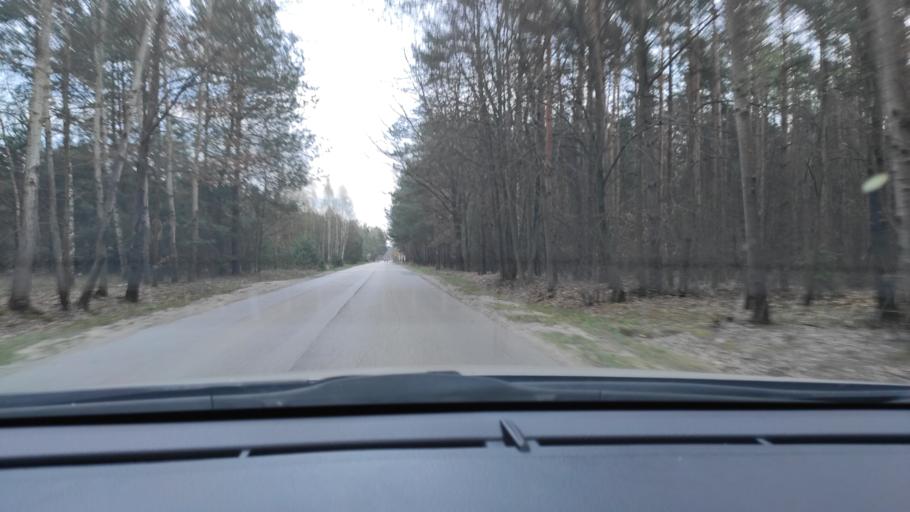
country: PL
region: Masovian Voivodeship
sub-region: Powiat radomski
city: Pionki
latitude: 51.5402
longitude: 21.3915
